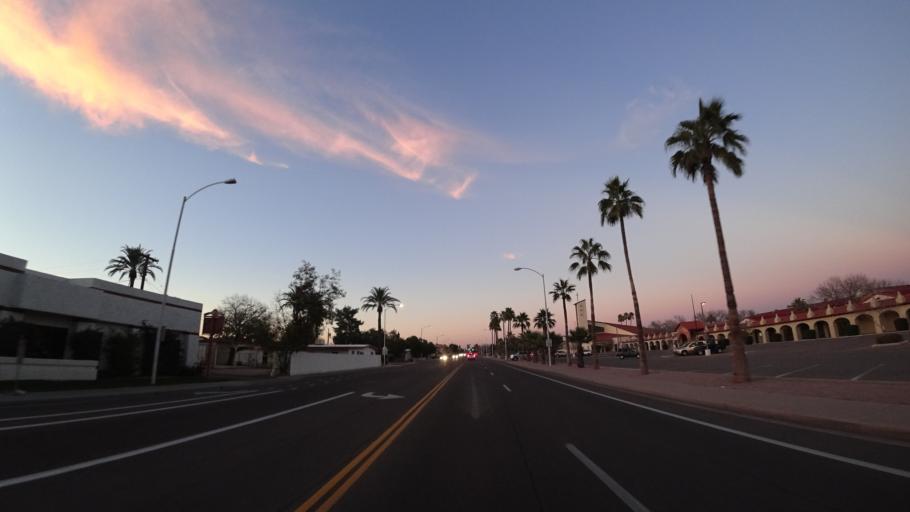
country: US
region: Arizona
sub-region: Maricopa County
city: Scottsdale
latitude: 33.4915
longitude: -111.9175
